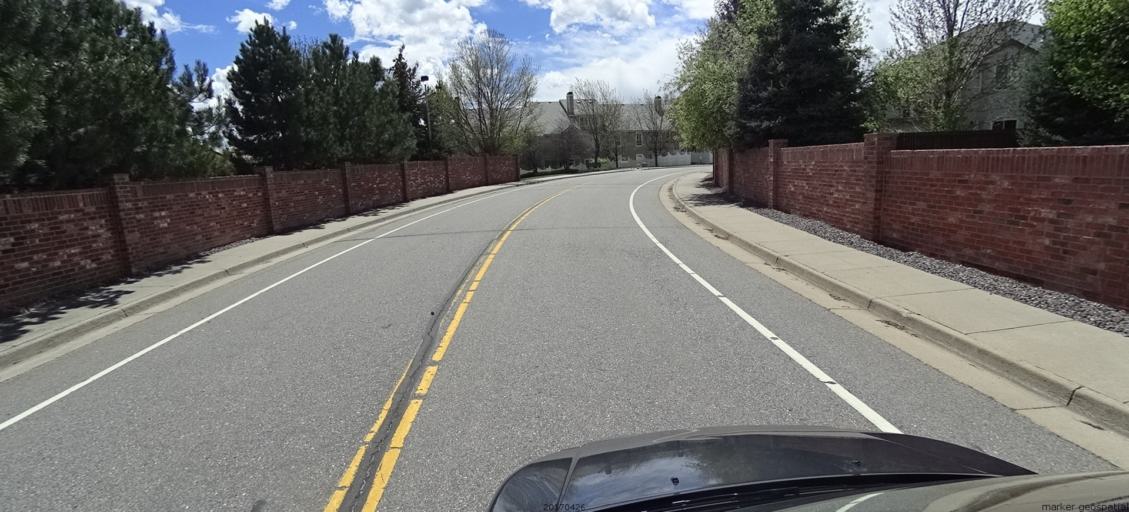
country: US
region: Colorado
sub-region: Douglas County
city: Carriage Club
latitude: 39.5392
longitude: -104.8914
